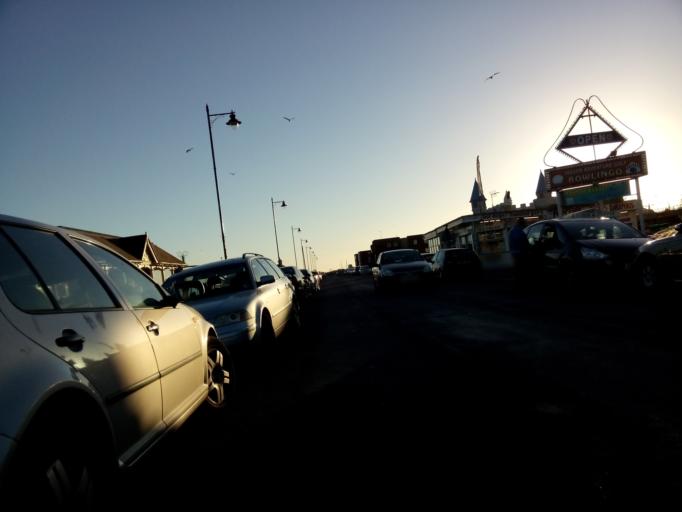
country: GB
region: England
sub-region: Suffolk
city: Felixstowe
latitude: 51.9527
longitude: 1.3394
